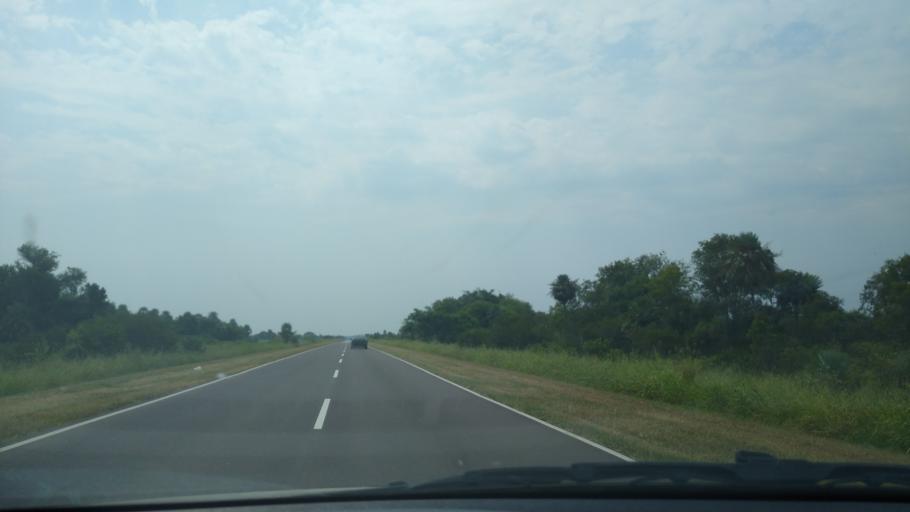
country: AR
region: Chaco
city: La Eduvigis
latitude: -27.0047
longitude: -58.9716
